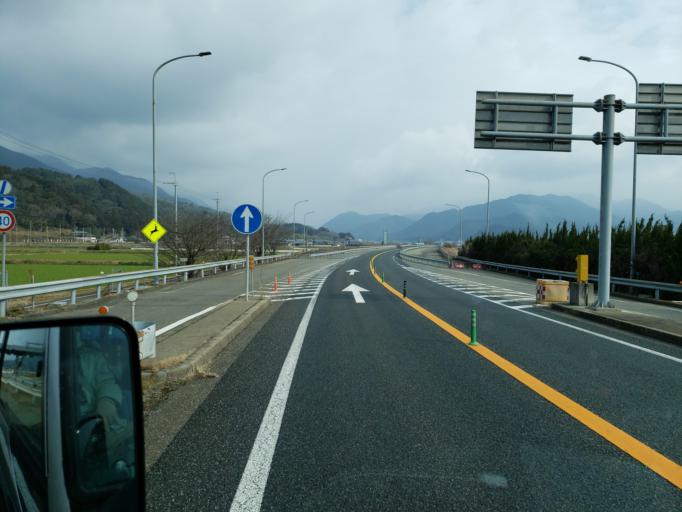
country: JP
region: Hyogo
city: Yamazakicho-nakabirose
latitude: 35.0595
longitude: 134.7643
